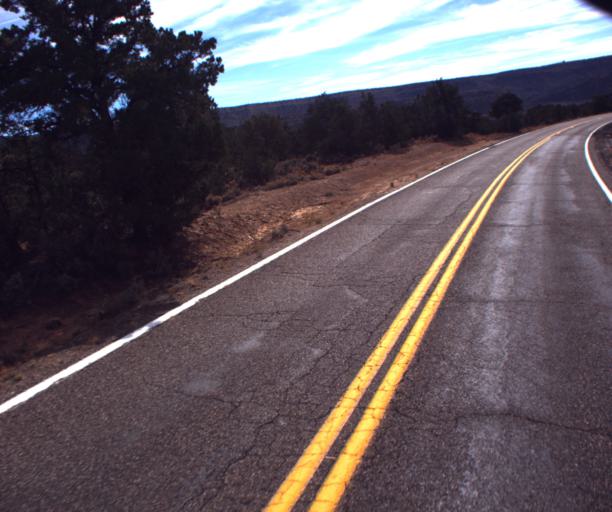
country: US
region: Arizona
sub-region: Navajo County
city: Kayenta
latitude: 36.5849
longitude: -110.4906
